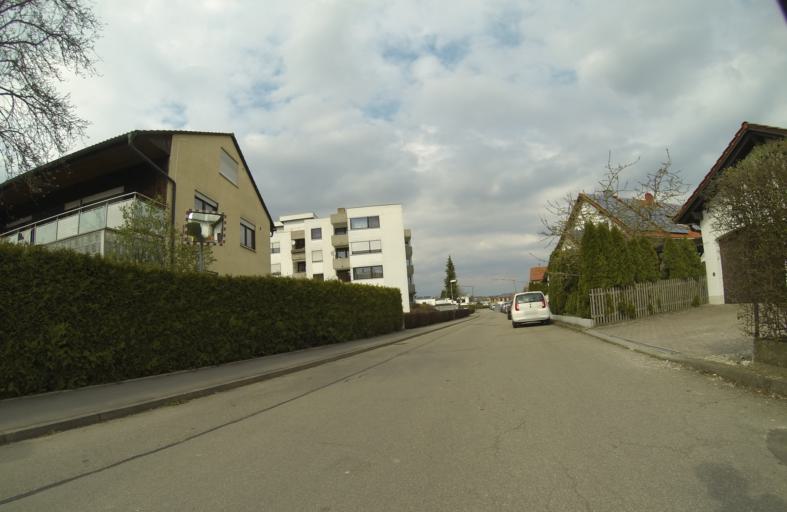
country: DE
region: Baden-Wuerttemberg
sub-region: Tuebingen Region
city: Erbach
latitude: 48.3048
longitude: 9.9024
